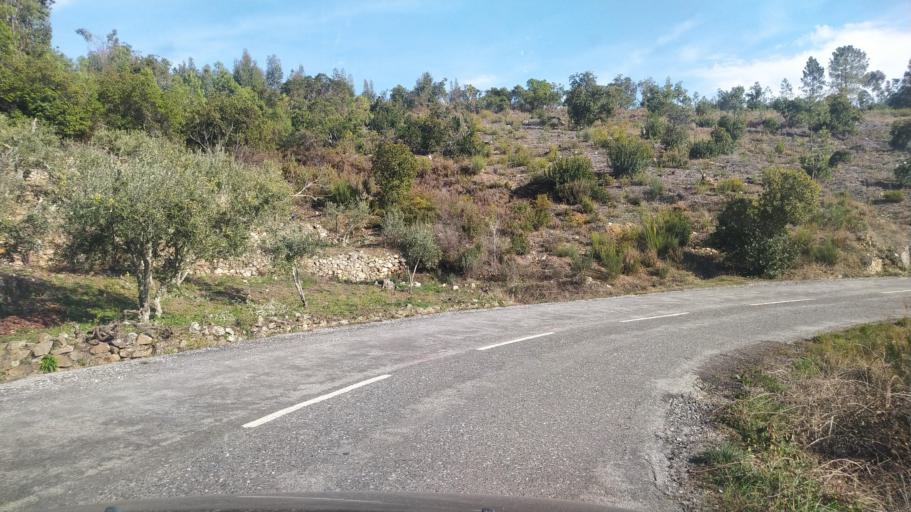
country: PT
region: Coimbra
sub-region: Oliveira do Hospital
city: Oliveira do Hospital
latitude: 40.1981
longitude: -7.7273
